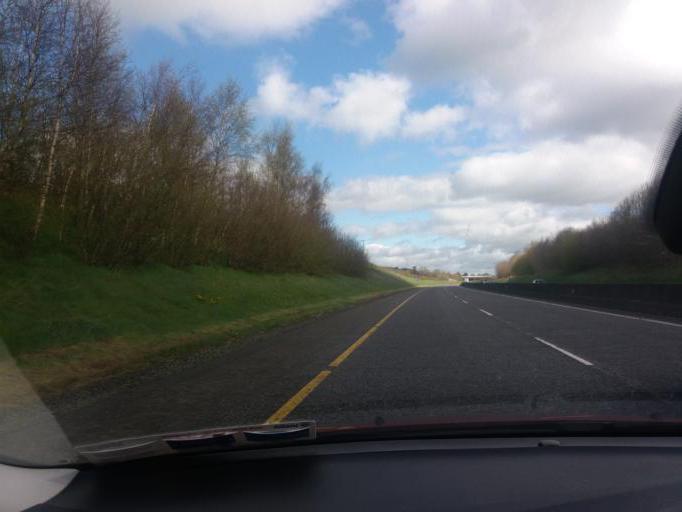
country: IE
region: Munster
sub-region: County Cork
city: Rathcormac
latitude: 52.0751
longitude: -8.3020
